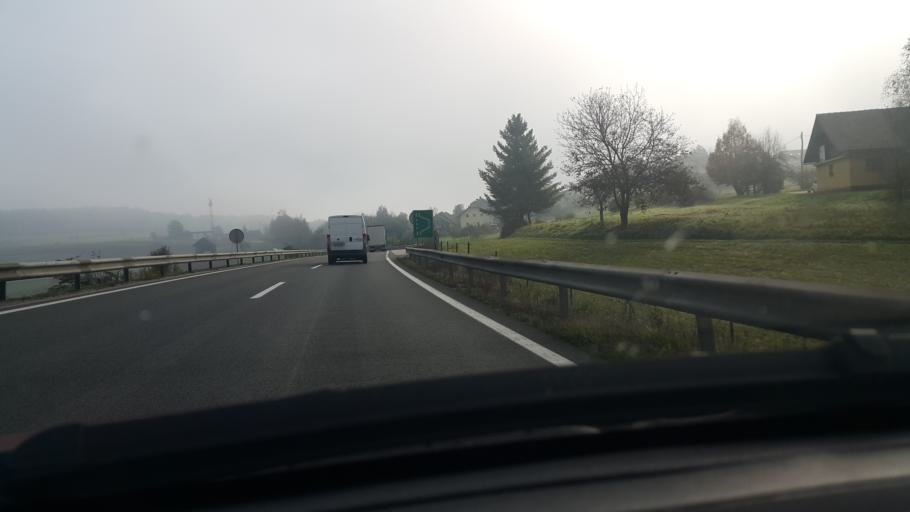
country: SI
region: Grosuplje
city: Grosuplje
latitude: 45.9621
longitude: 14.7171
